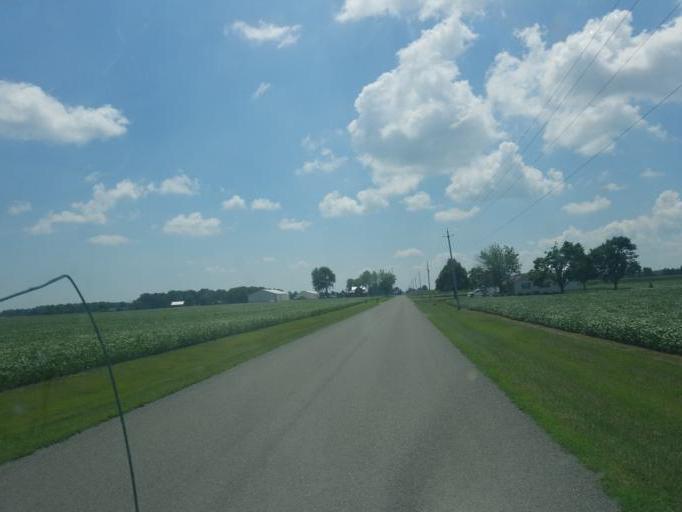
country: US
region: Ohio
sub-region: Mercer County
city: Celina
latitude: 40.5889
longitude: -84.4939
